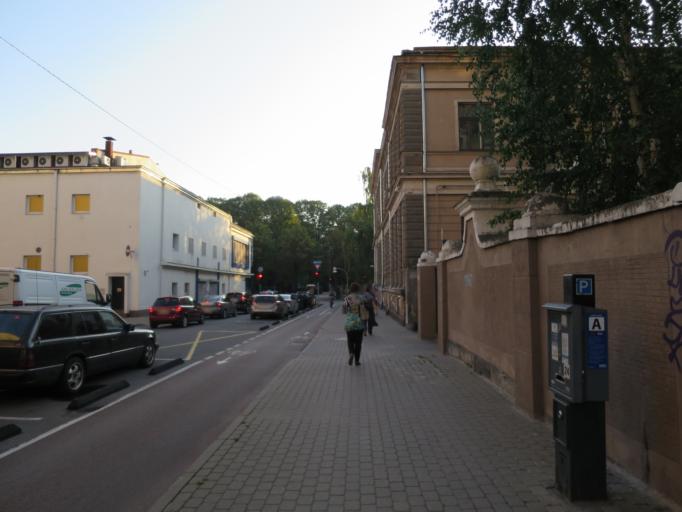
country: LV
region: Riga
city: Riga
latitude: 56.9562
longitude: 24.1159
